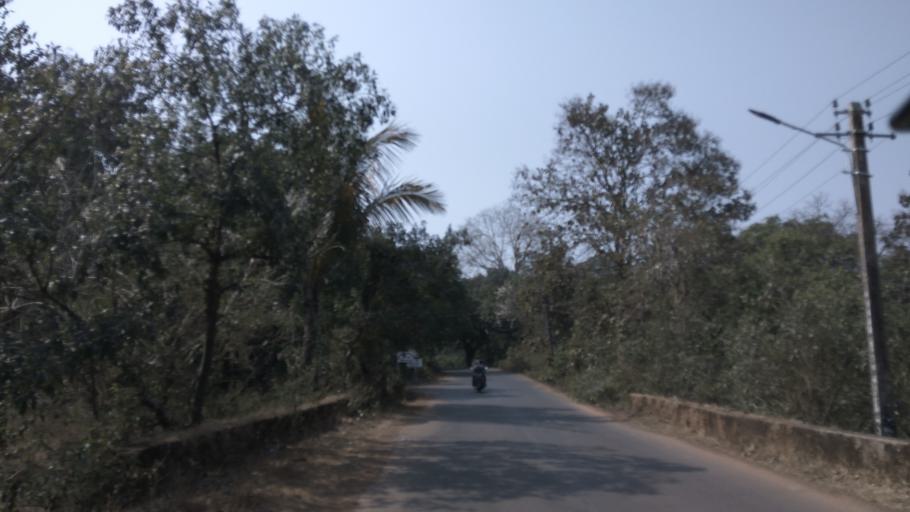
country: IN
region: Goa
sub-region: South Goa
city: Sanvordem
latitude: 15.3467
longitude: 74.2370
